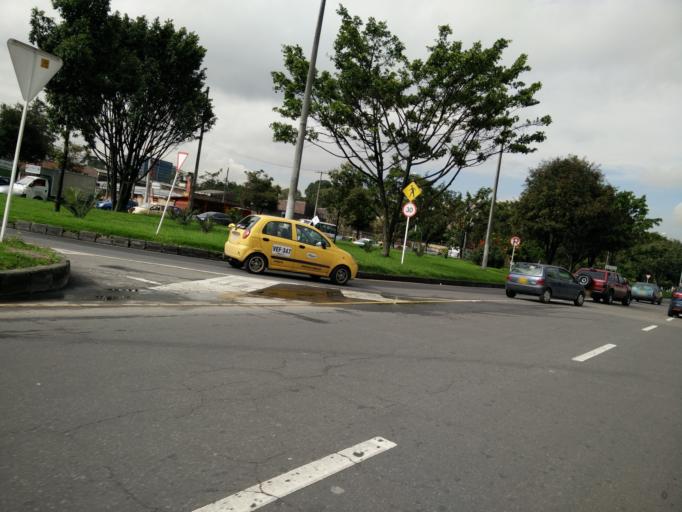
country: CO
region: Bogota D.C.
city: Bogota
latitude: 4.6662
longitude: -74.1064
